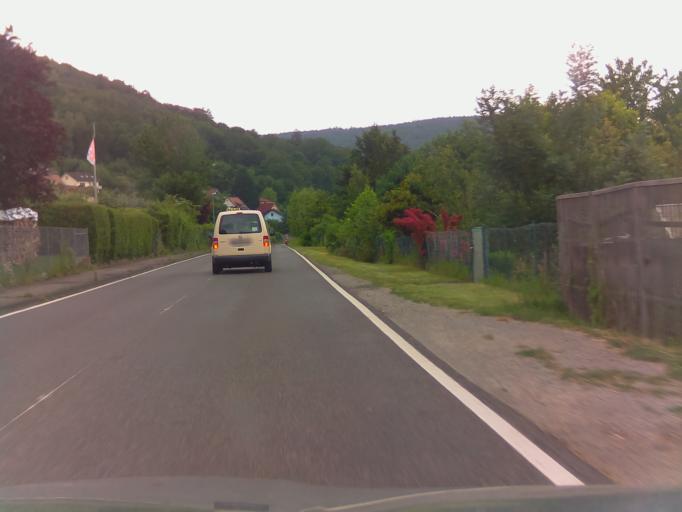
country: DE
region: Bavaria
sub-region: Regierungsbezirk Unterfranken
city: Gemunden
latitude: 50.0641
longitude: 9.7018
